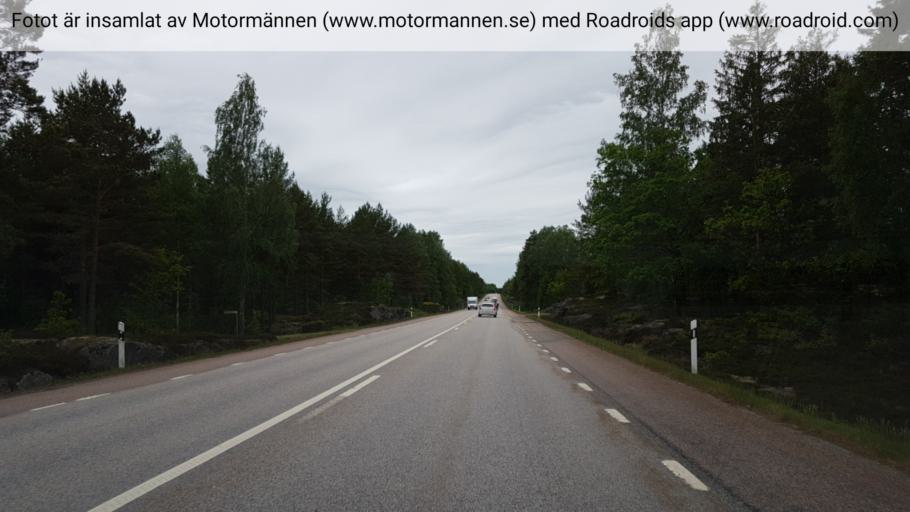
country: SE
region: Kalmar
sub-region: Oskarshamns Kommun
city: Oskarshamn
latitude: 57.4516
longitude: 16.5078
